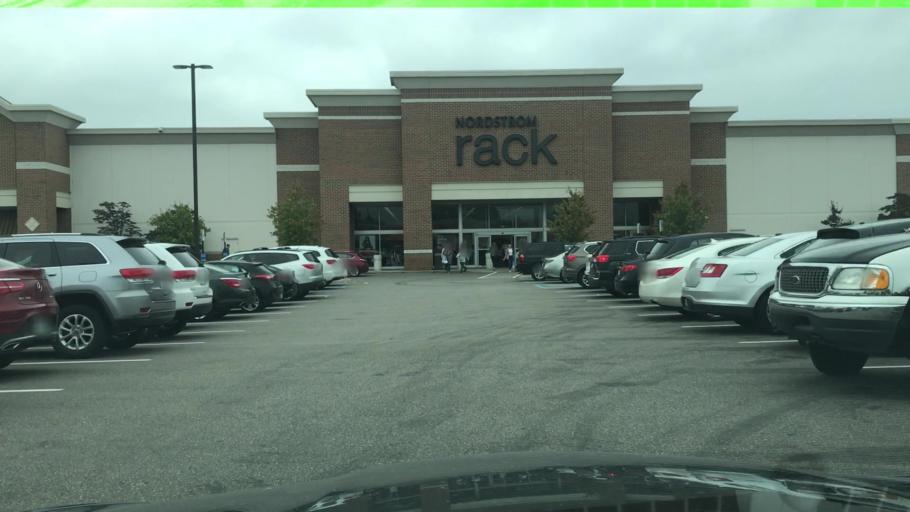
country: US
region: Michigan
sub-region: Oakland County
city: Clawson
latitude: 42.5618
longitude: -83.1312
